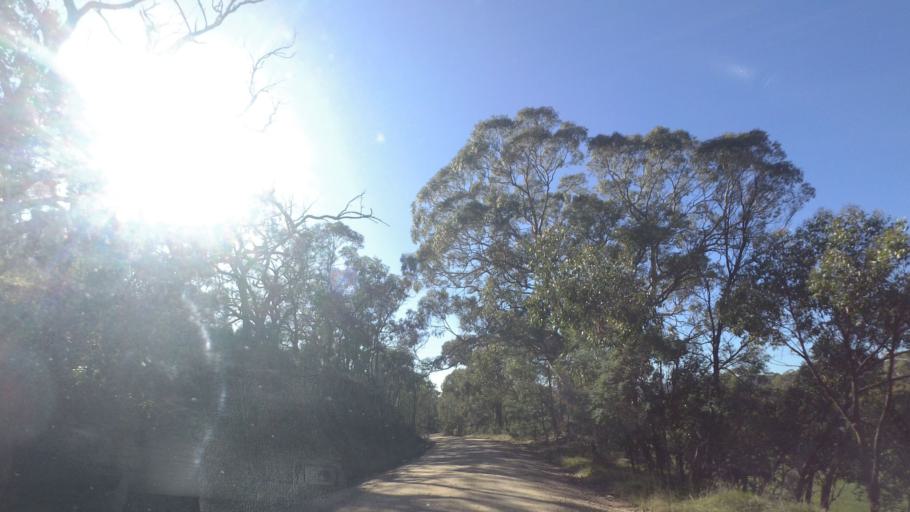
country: AU
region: Victoria
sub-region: Mount Alexander
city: Castlemaine
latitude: -37.1217
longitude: 144.4117
